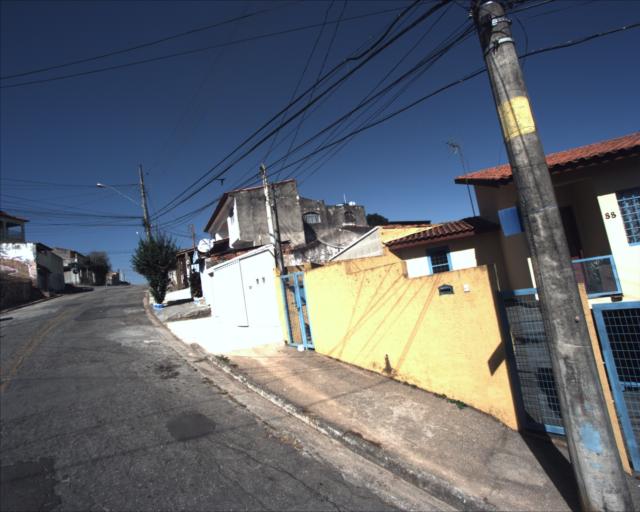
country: BR
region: Sao Paulo
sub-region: Sorocaba
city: Sorocaba
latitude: -23.5015
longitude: -47.4415
